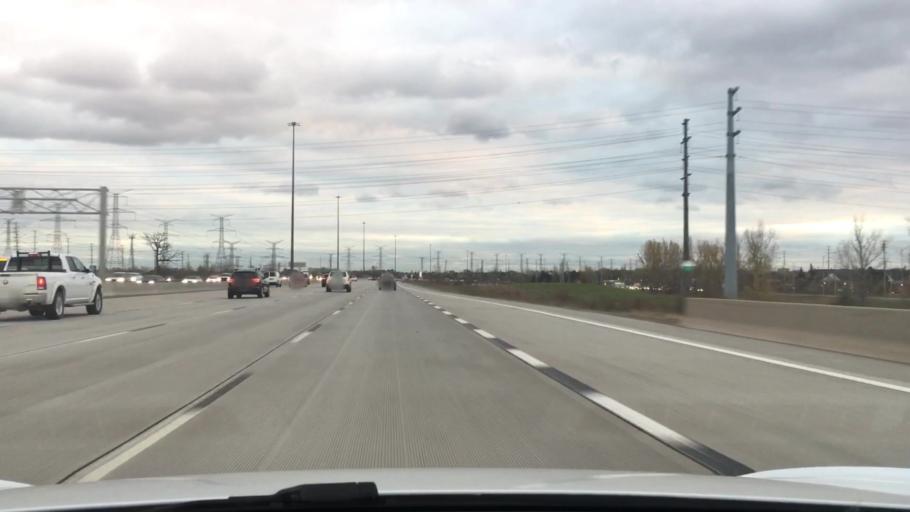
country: CA
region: Ontario
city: Concord
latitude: 43.8118
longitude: -79.4801
